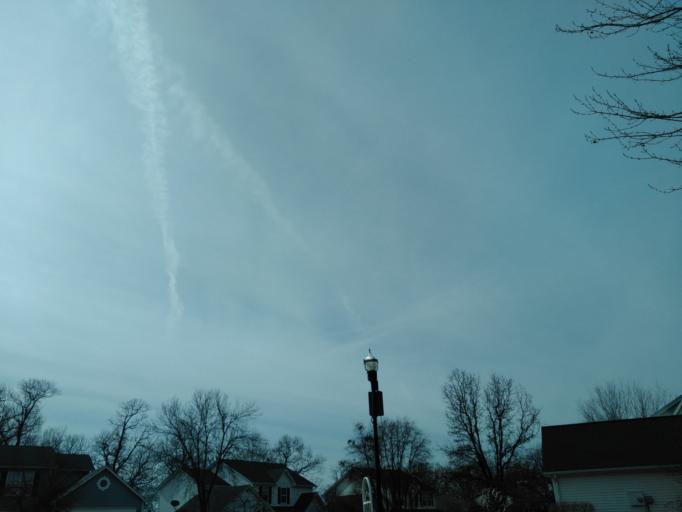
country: US
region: Missouri
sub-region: Saint Louis County
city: Valley Park
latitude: 38.5494
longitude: -90.5177
